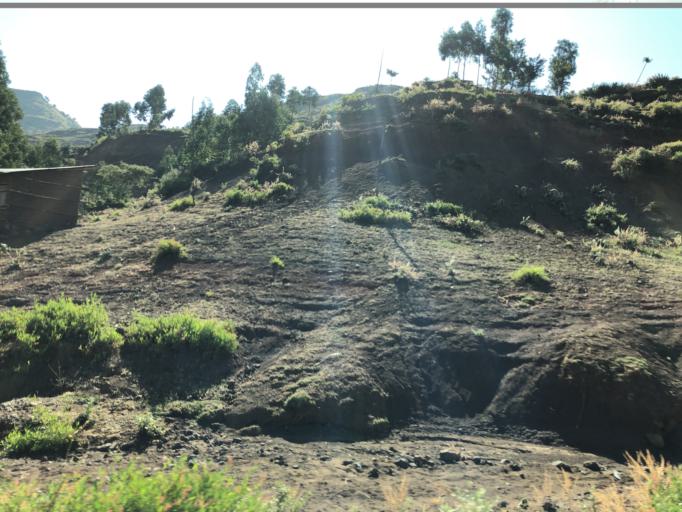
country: ET
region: Amhara
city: Lalibela
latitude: 12.0111
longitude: 39.0521
